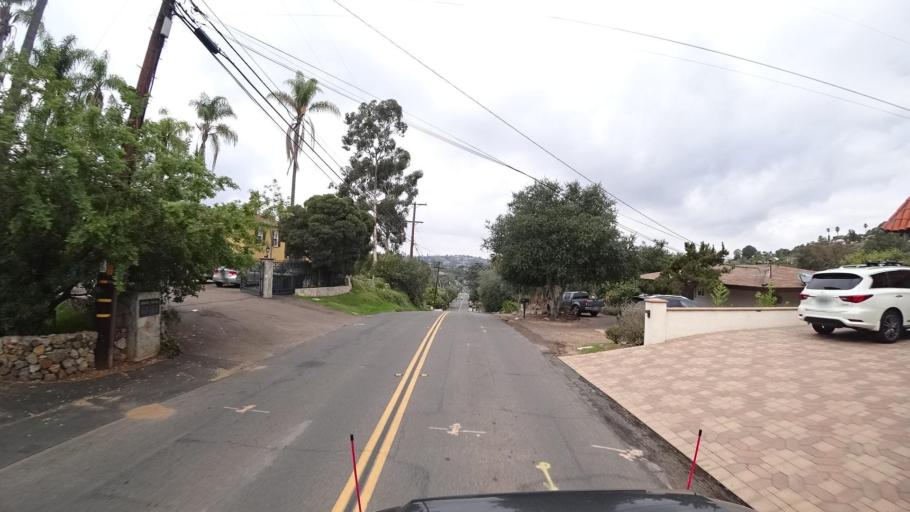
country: US
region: California
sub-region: San Diego County
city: Spring Valley
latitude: 32.7579
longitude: -116.9945
